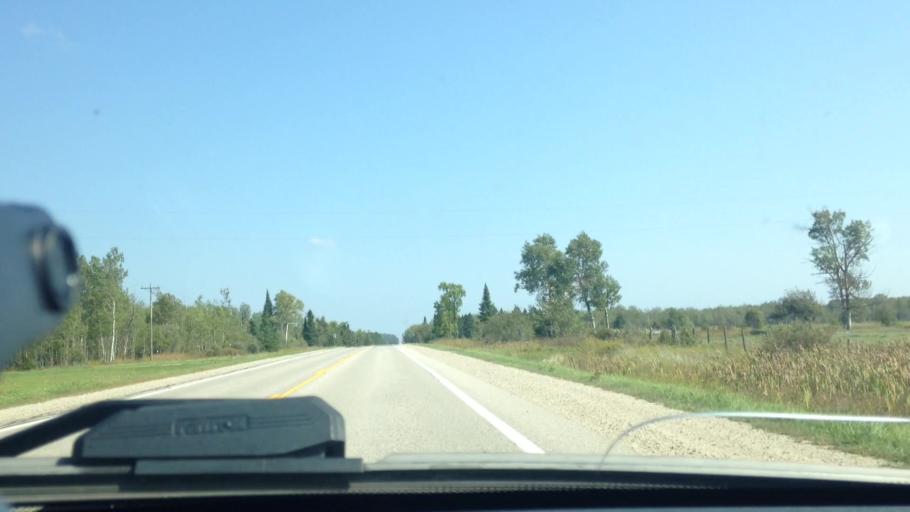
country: US
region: Michigan
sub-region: Luce County
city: Newberry
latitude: 46.3105
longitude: -85.6005
